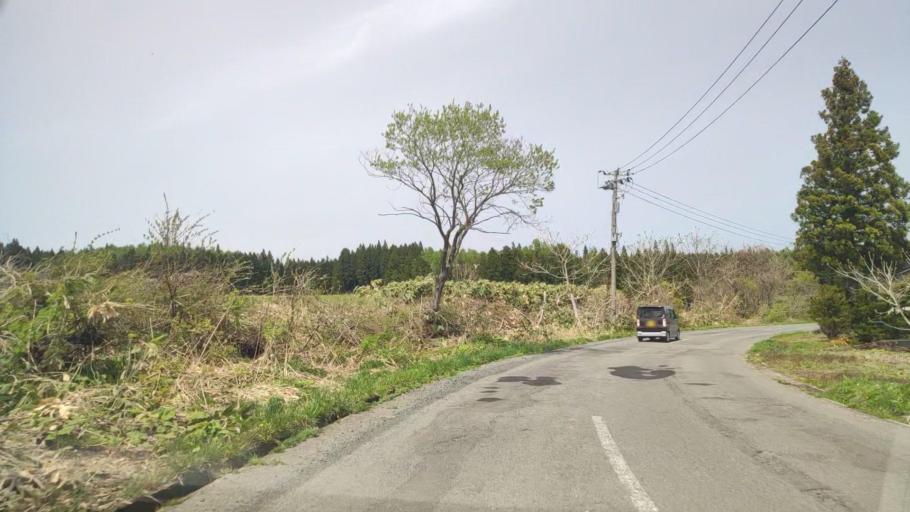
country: JP
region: Aomori
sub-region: Misawa Shi
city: Inuotose
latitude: 40.7655
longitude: 141.1189
